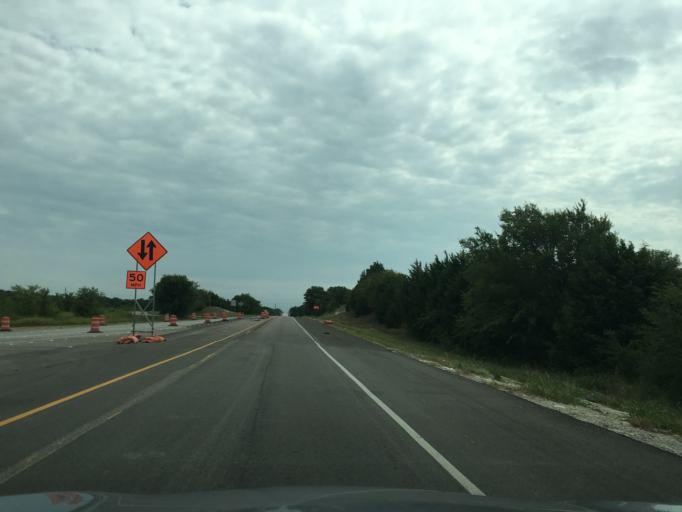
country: US
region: Texas
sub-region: Collin County
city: Anna
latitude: 33.3147
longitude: -96.5090
